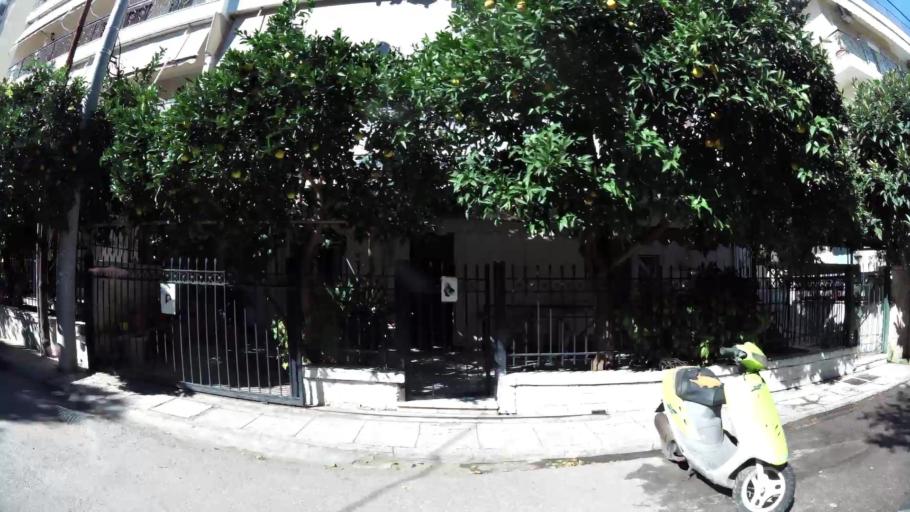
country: GR
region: Attica
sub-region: Nomarchia Athinas
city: Khalandrion
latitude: 38.0331
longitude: 23.8125
